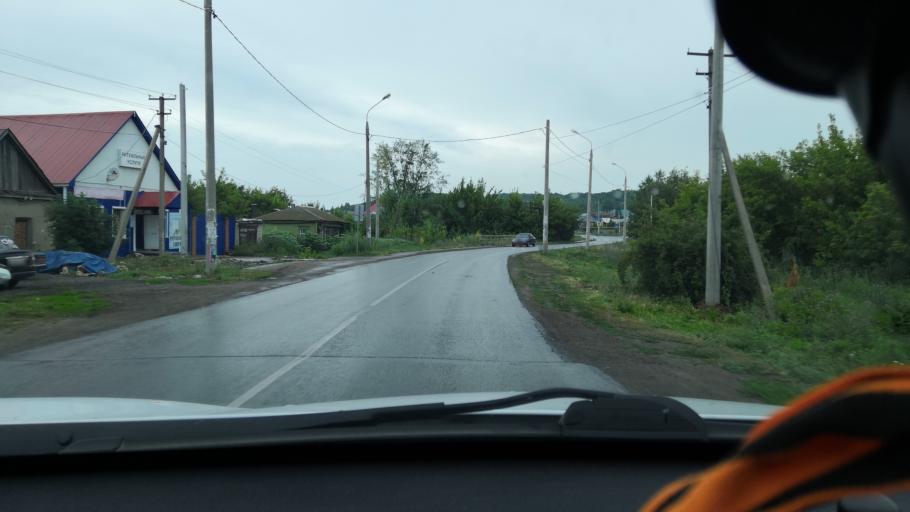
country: RU
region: Samara
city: Novosemeykino
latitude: 53.3776
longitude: 50.3487
